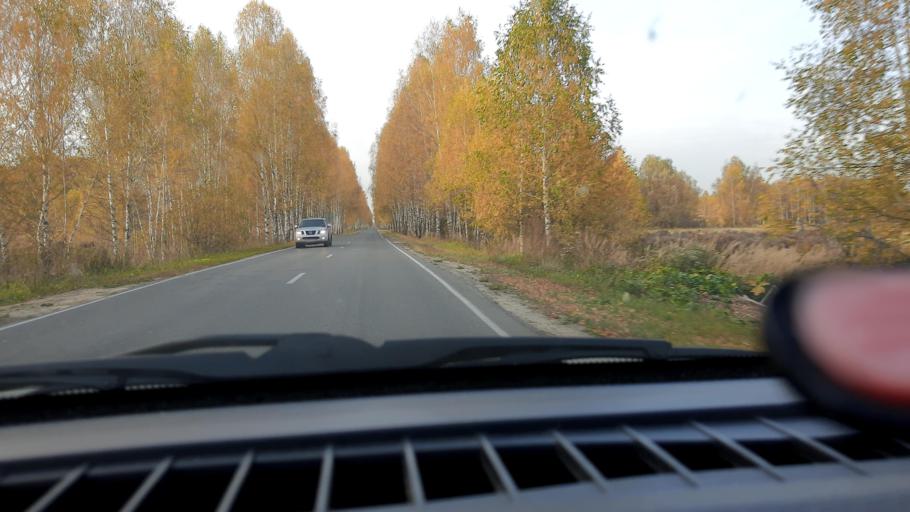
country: RU
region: Nizjnij Novgorod
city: Neklyudovo
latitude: 56.4823
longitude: 43.8691
